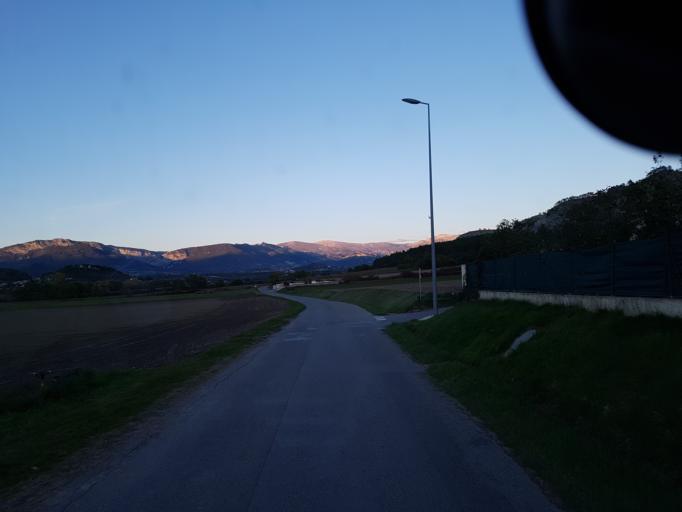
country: FR
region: Provence-Alpes-Cote d'Azur
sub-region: Departement des Alpes-de-Haute-Provence
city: Peipin
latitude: 44.1219
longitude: 5.9550
